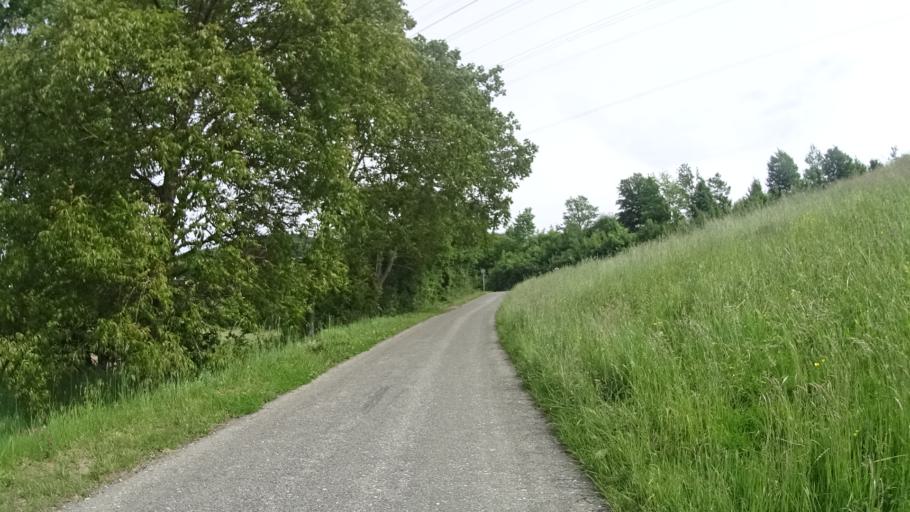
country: CH
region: Aargau
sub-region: Bezirk Rheinfelden
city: Mohlin
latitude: 47.5473
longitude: 7.8640
